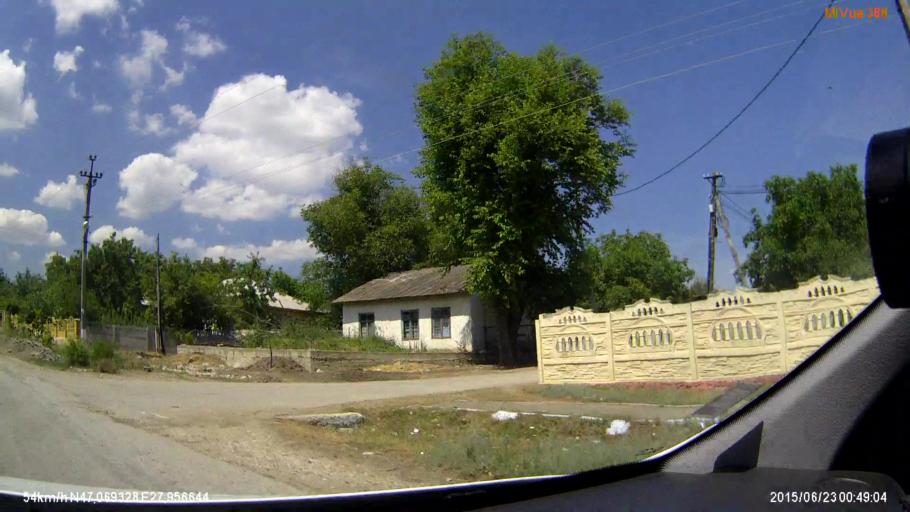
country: RO
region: Iasi
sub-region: Comuna Prisacani
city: Prisacani
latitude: 47.0692
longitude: 27.9568
